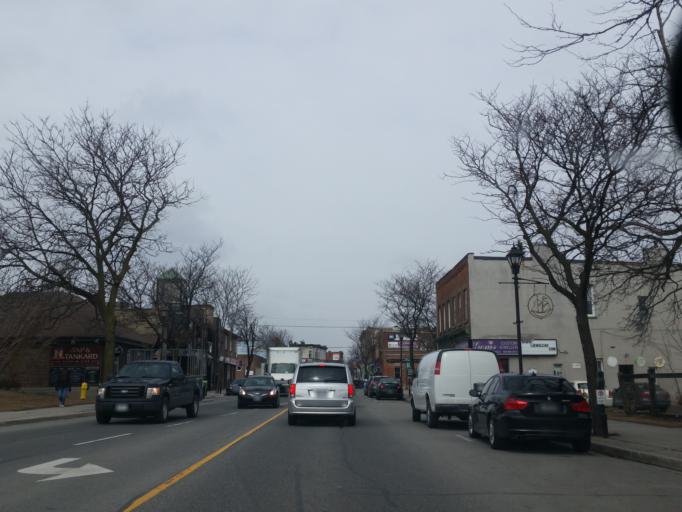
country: CA
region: Ontario
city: Oshawa
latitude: 43.8780
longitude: -78.9414
